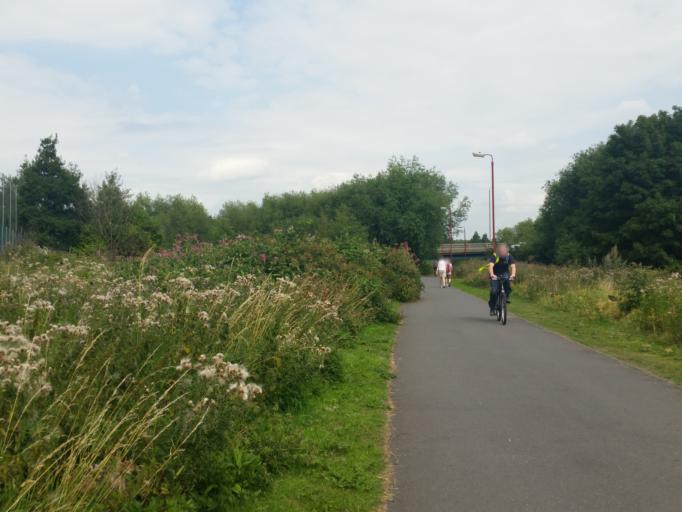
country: GB
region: England
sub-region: Derby
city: Derby
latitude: 52.9162
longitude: -1.4433
